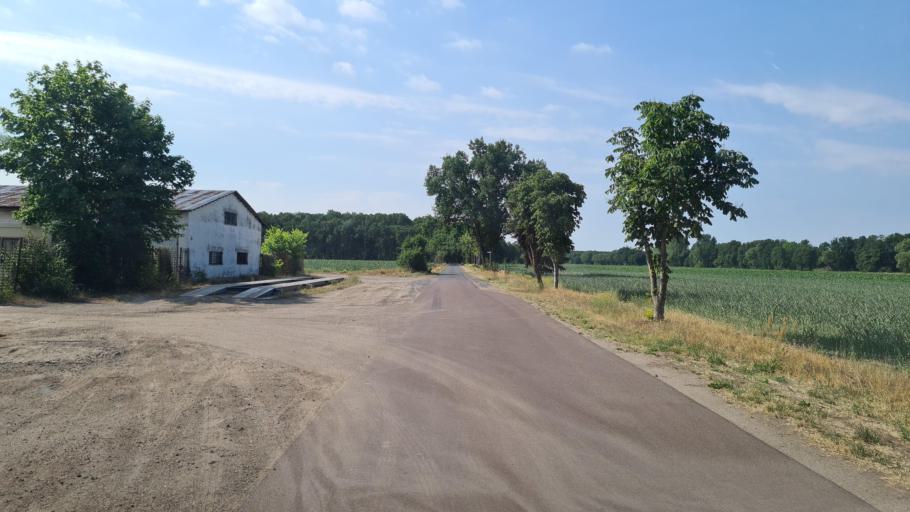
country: DE
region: Brandenburg
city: Brandenburg an der Havel
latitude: 52.3342
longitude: 12.5449
